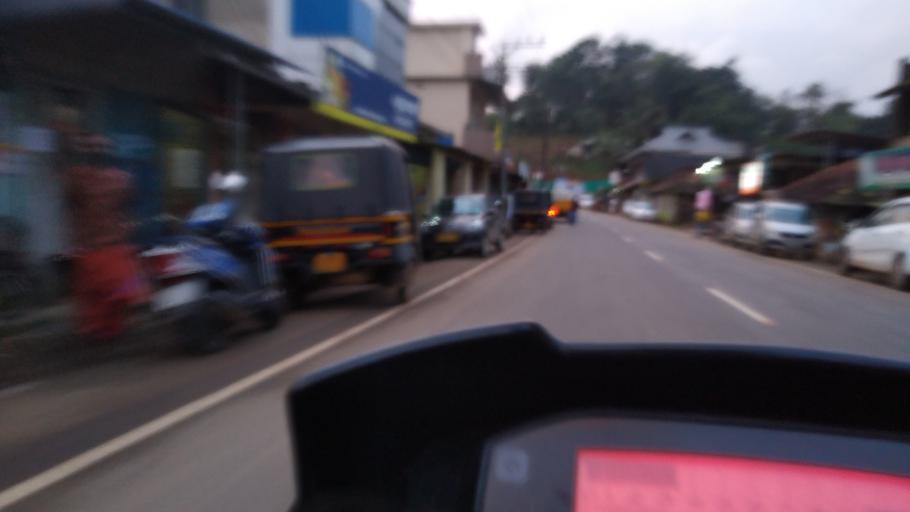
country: IN
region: Kerala
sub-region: Idukki
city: Munnar
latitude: 9.9687
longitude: 77.1144
